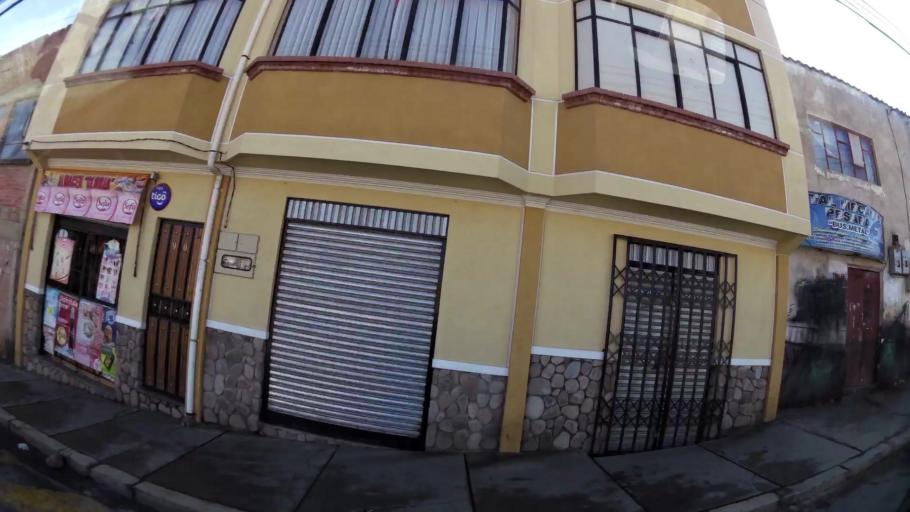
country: BO
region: La Paz
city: La Paz
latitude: -16.5081
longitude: -68.1106
